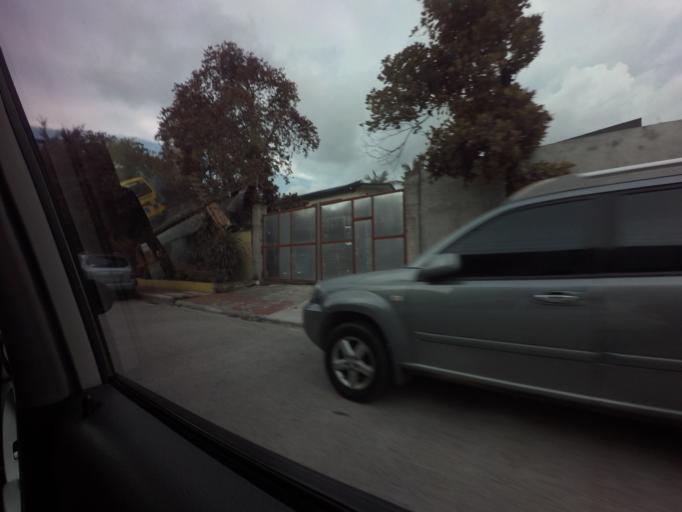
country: PH
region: Metro Manila
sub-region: City of Manila
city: Manila
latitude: 14.6166
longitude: 121.0044
